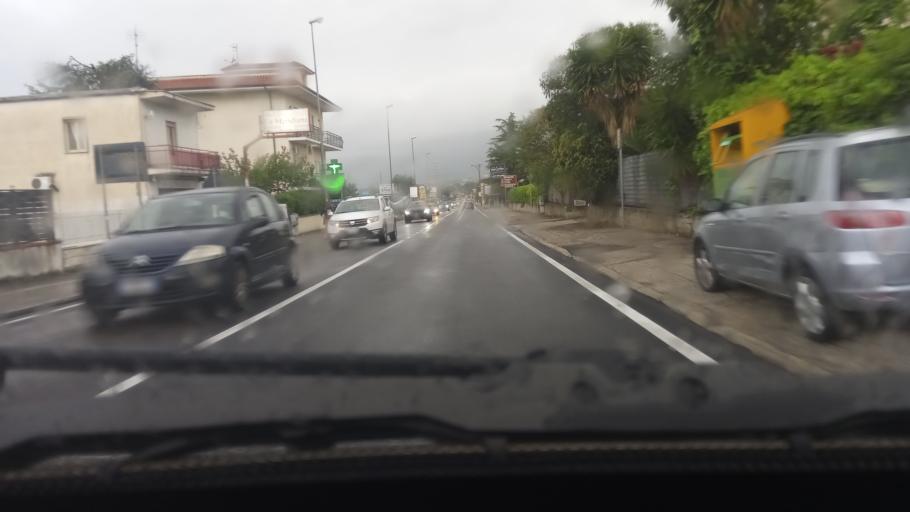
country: IT
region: Latium
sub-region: Provincia di Latina
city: Penitro
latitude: 41.2609
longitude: 13.6896
